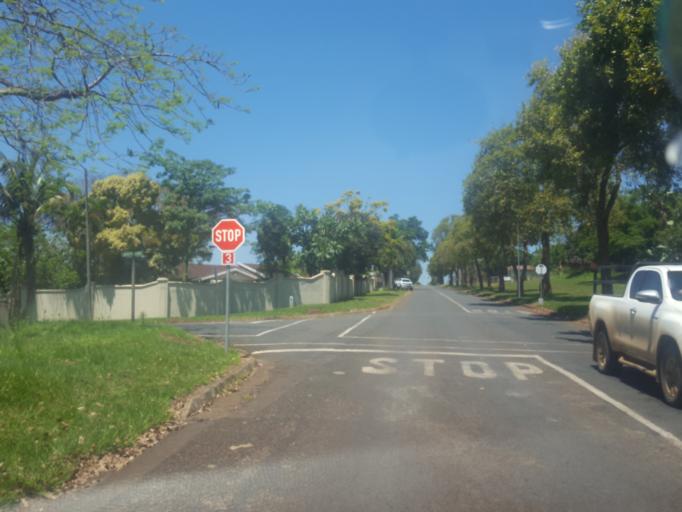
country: ZA
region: KwaZulu-Natal
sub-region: uThungulu District Municipality
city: Empangeni
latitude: -28.7519
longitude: 31.9023
